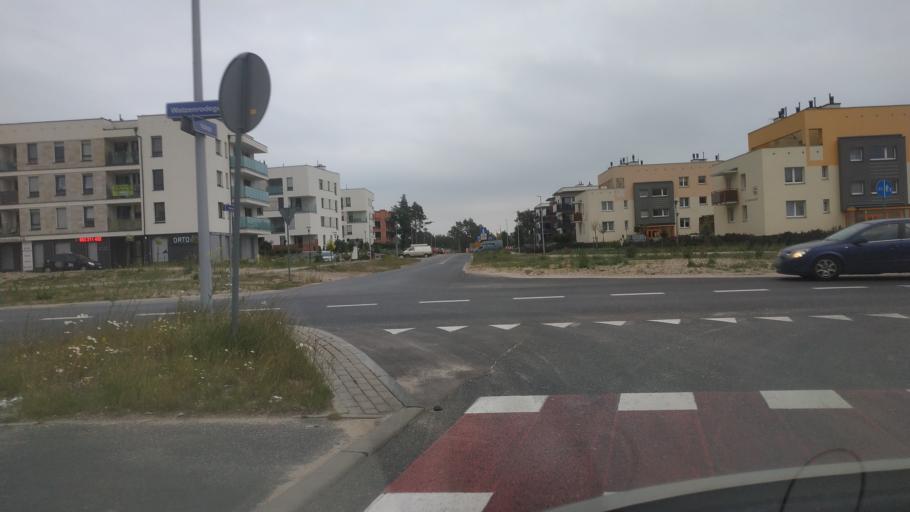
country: PL
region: Kujawsko-Pomorskie
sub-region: Torun
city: Torun
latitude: 53.0468
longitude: 18.6031
